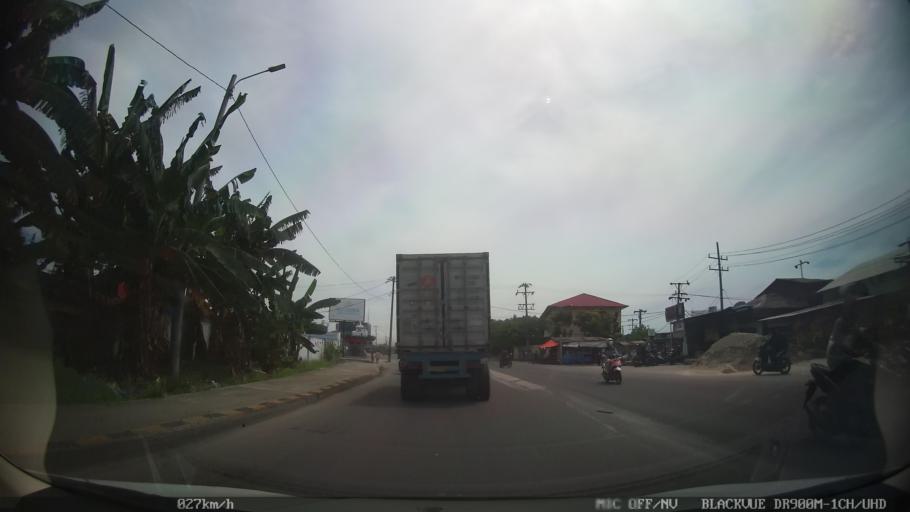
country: ID
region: North Sumatra
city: Belawan
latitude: 3.7771
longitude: 98.7017
